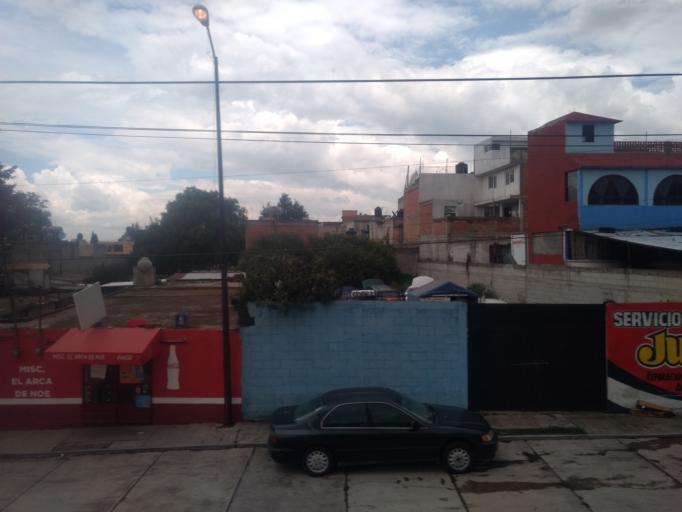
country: MX
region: Tlaxcala
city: Apizaco
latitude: 19.4224
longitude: -98.1395
